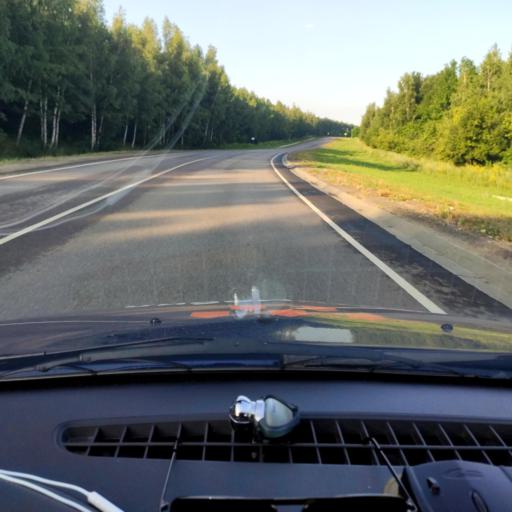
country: RU
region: Lipetsk
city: Izmalkovo
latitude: 52.4578
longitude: 38.0094
